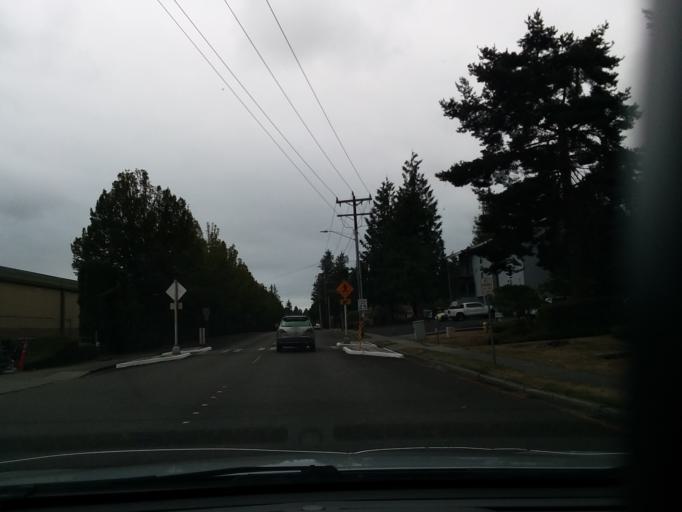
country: US
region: Washington
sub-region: Snohomish County
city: Alderwood Manor
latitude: 47.8228
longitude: -122.2938
